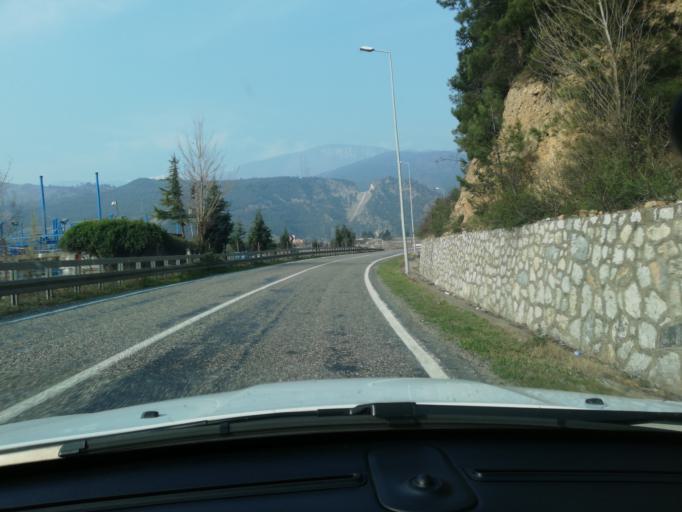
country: TR
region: Karabuk
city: Karabuk
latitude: 41.1560
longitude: 32.5411
